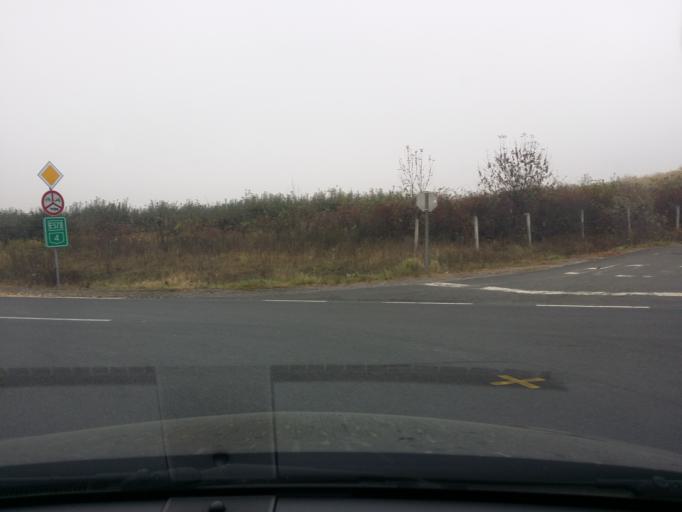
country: HU
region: Szabolcs-Szatmar-Bereg
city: Nyirbogdany
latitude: 48.0205
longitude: 21.8430
